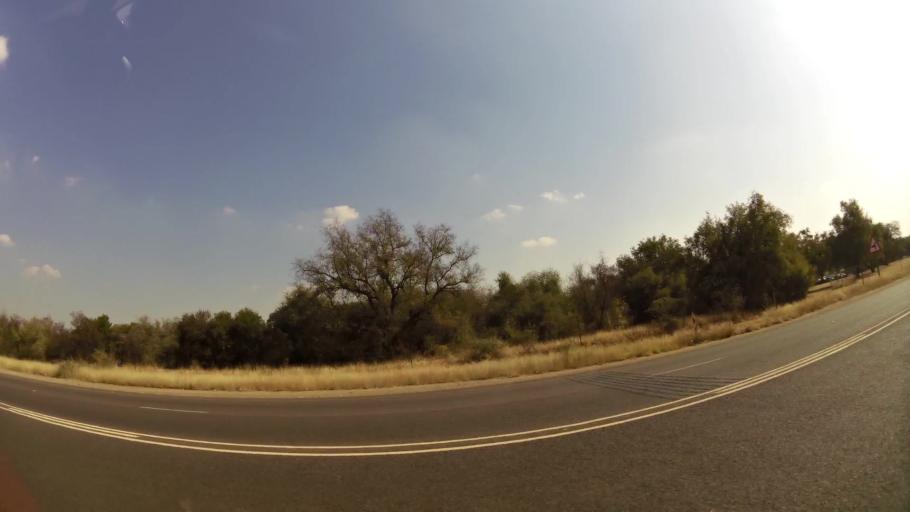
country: ZA
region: North-West
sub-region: Bojanala Platinum District Municipality
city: Mogwase
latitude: -25.4320
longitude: 27.0824
